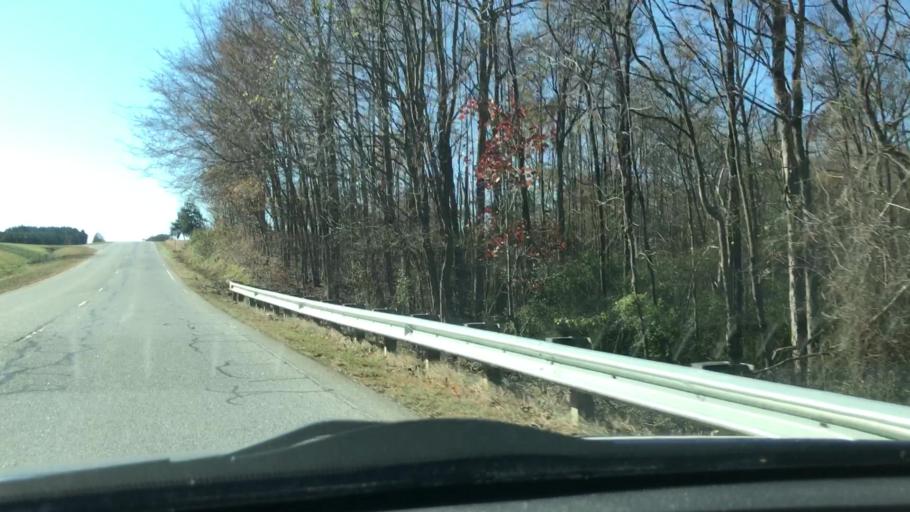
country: US
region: North Carolina
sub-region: Davidson County
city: Denton
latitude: 35.5905
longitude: -80.0478
